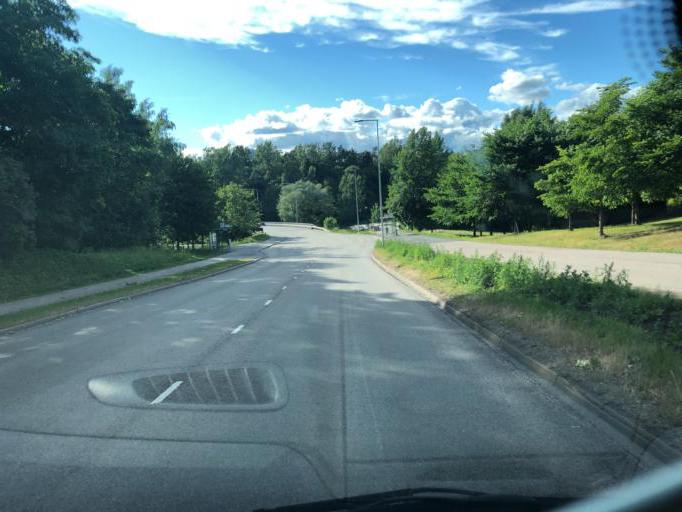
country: FI
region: Uusimaa
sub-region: Helsinki
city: Vantaa
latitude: 60.2946
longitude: 25.0684
